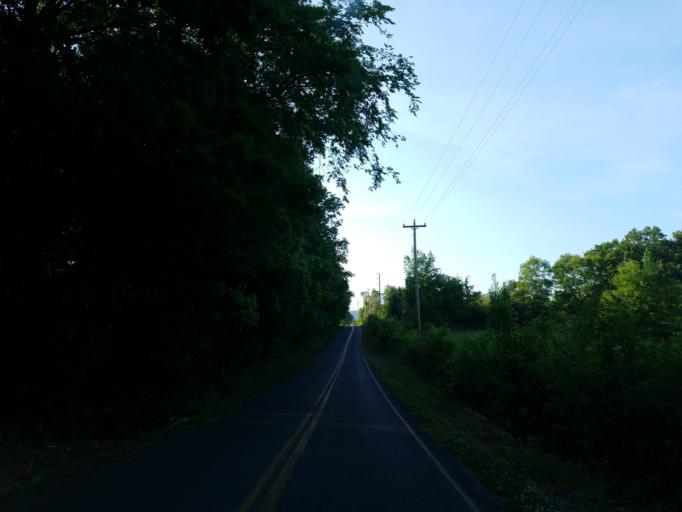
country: US
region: Georgia
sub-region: Gordon County
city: Calhoun
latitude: 34.5014
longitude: -85.1154
